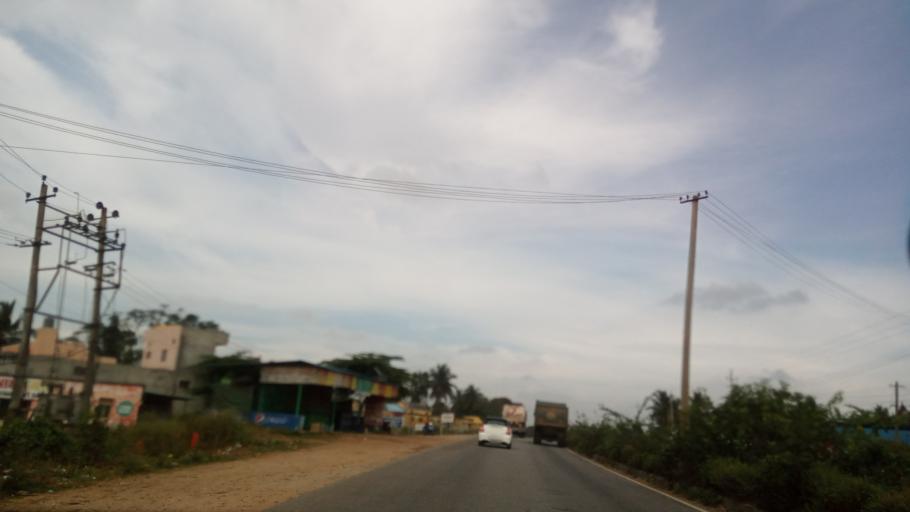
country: IN
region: Karnataka
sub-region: Mandya
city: Shrirangapattana
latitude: 12.4381
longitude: 76.7119
